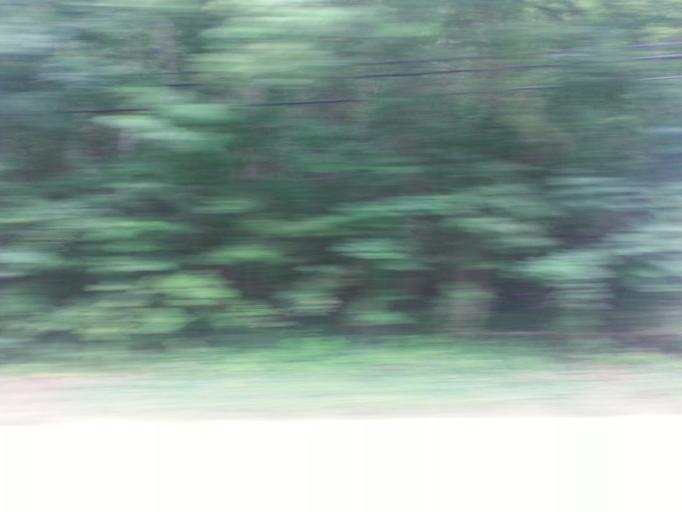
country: US
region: Ohio
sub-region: Brown County
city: Ripley
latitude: 38.7081
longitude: -83.8092
